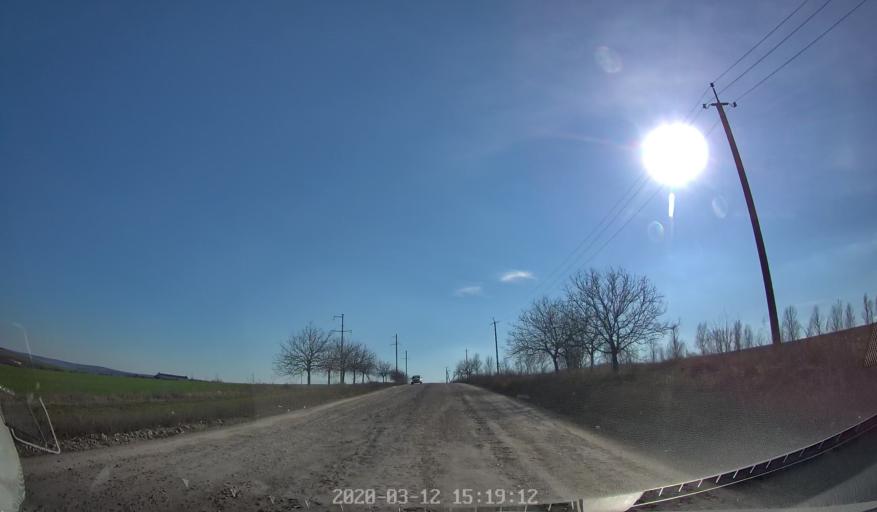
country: MD
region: Chisinau
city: Ciorescu
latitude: 47.2144
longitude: 28.9305
